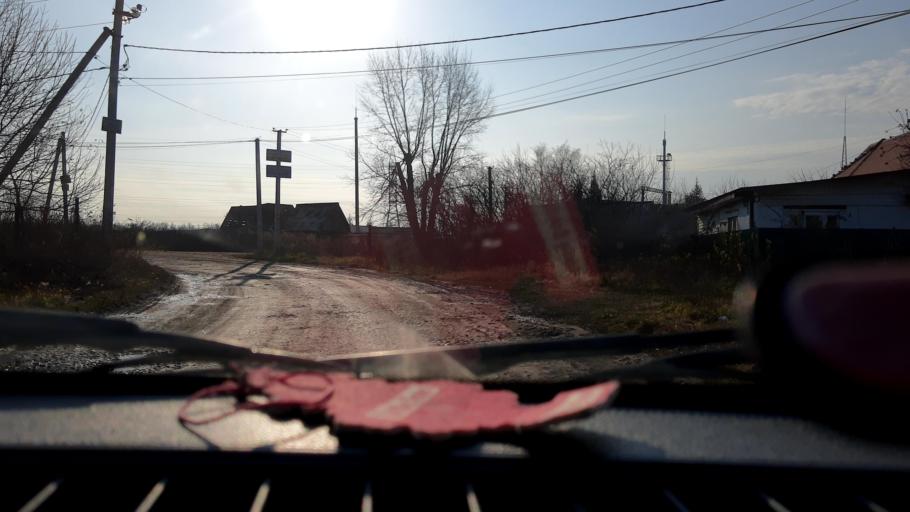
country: RU
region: Bashkortostan
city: Ufa
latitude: 54.6744
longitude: 56.0855
